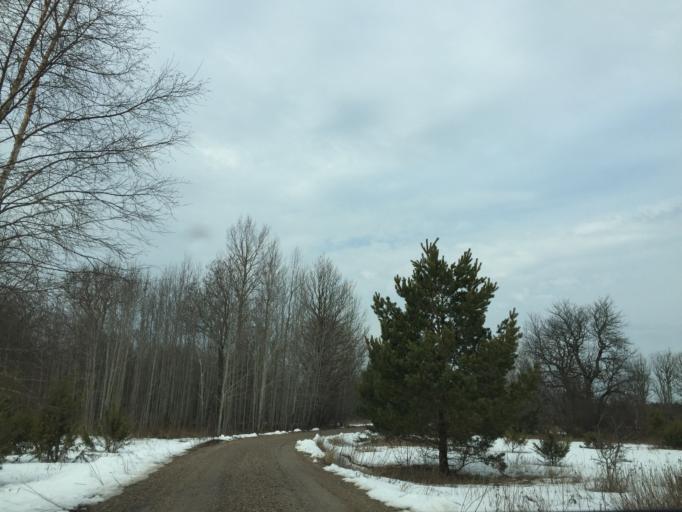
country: EE
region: Saare
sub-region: Kuressaare linn
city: Kuressaare
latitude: 58.4387
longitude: 22.1456
